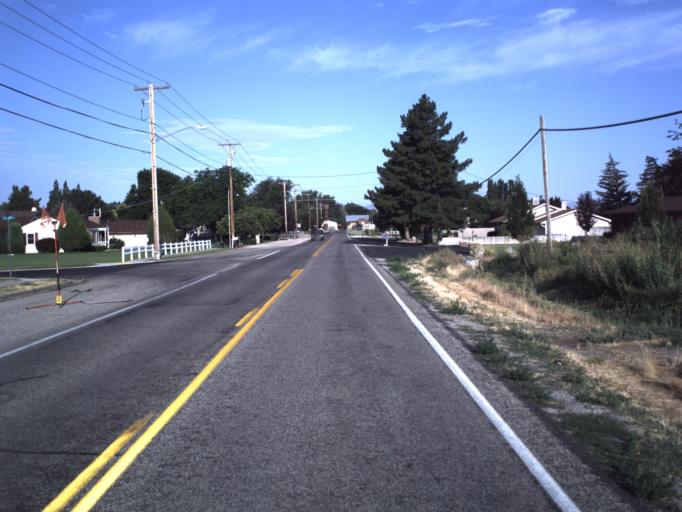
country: US
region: Utah
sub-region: Weber County
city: Plain City
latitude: 41.3053
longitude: -112.0752
